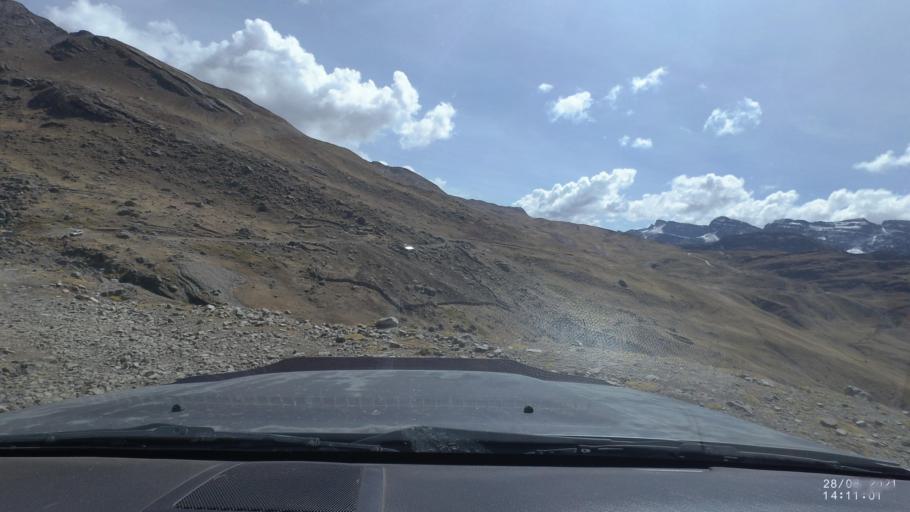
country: BO
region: Cochabamba
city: Sipe Sipe
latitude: -17.2602
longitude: -66.3834
